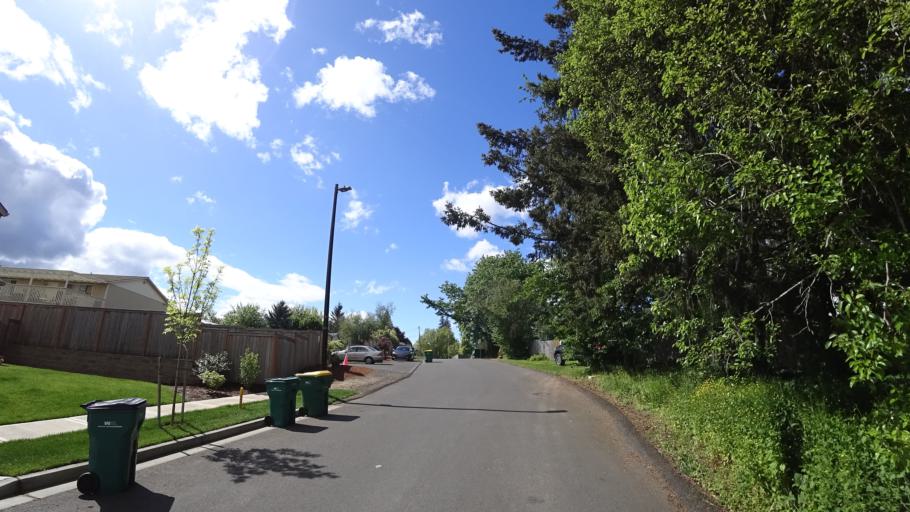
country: US
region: Oregon
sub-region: Washington County
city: Metzger
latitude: 45.4461
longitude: -122.7471
